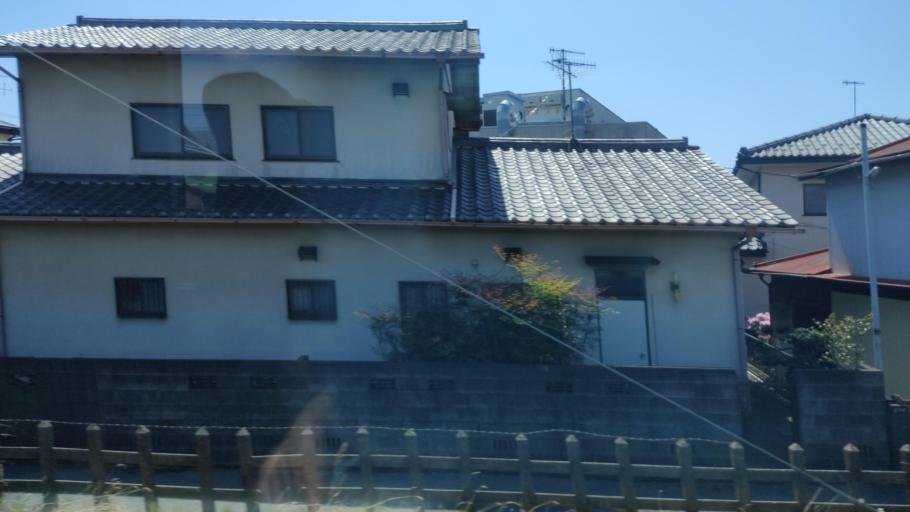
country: JP
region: Kanagawa
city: Chigasaki
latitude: 35.3276
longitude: 139.3930
